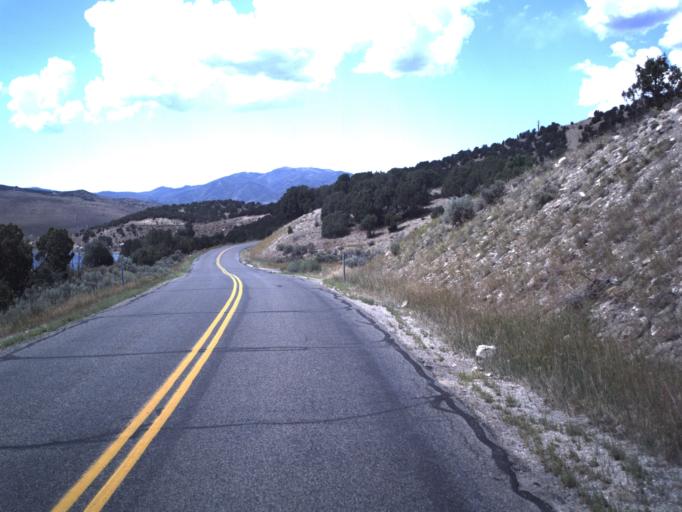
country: US
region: Utah
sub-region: Summit County
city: Oakley
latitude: 40.7595
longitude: -111.3752
